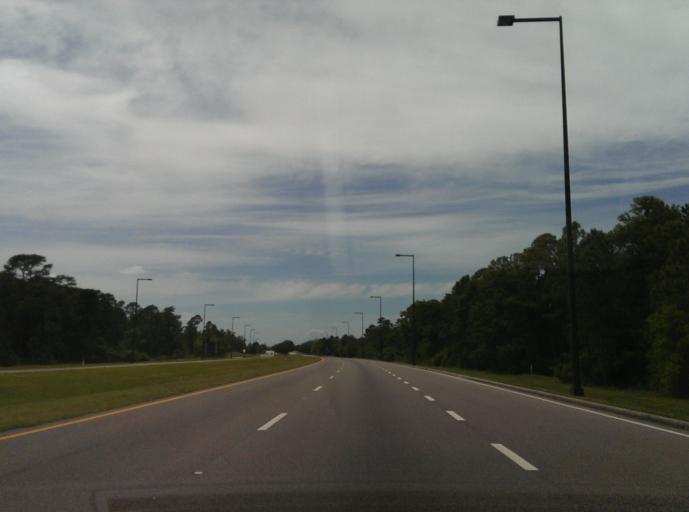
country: US
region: Florida
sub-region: Osceola County
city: Celebration
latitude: 28.3483
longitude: -81.5540
